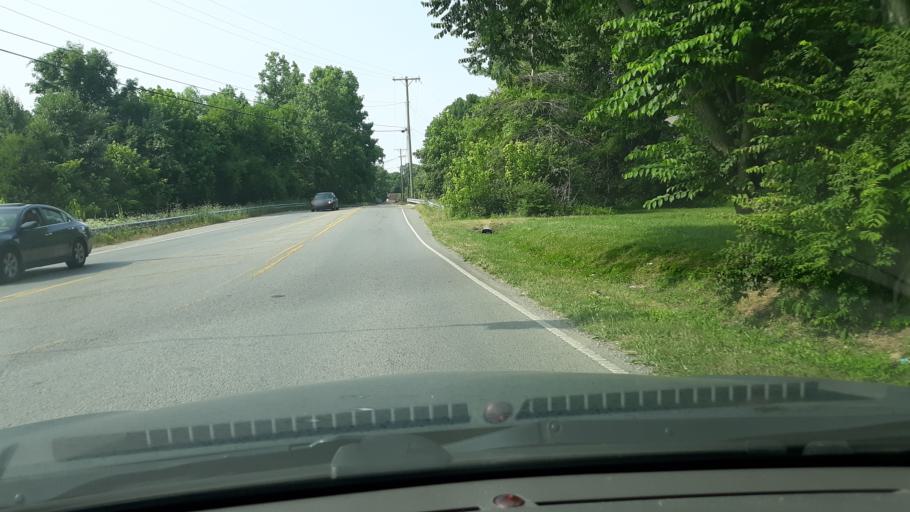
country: US
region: Tennessee
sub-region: Davidson County
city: Lakewood
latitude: 36.1781
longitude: -86.6138
